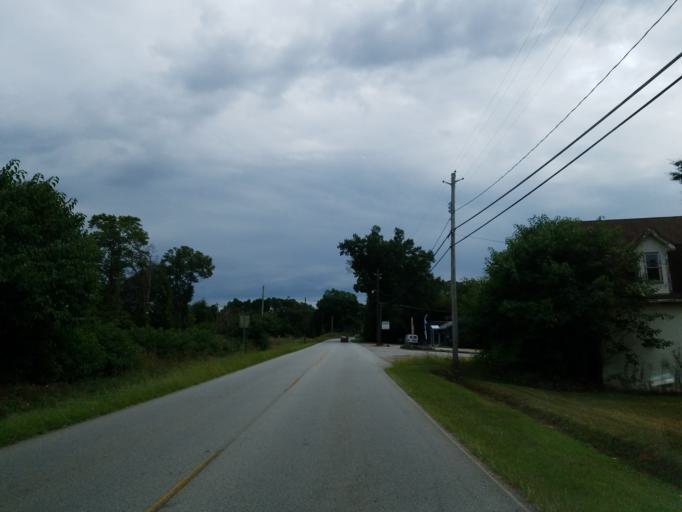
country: US
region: Georgia
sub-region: Spalding County
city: Experiment
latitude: 33.2810
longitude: -84.2833
